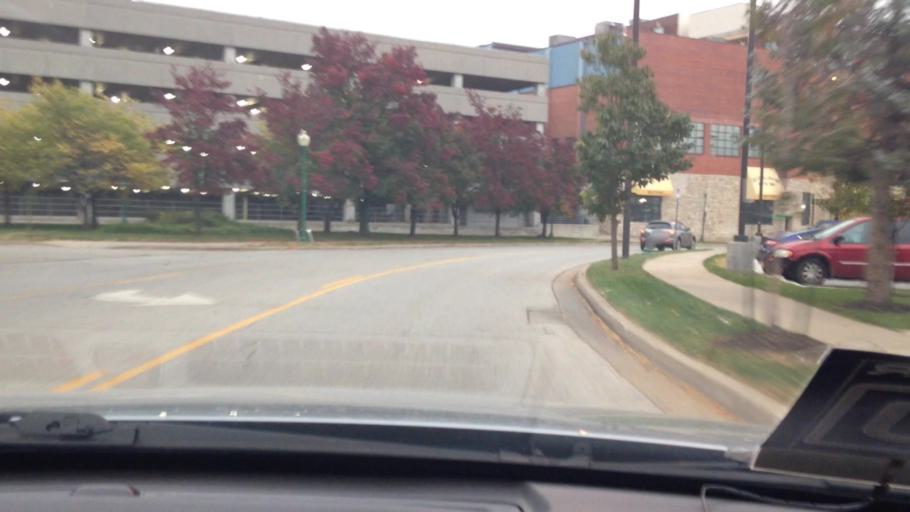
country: US
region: Kansas
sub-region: Johnson County
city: Westwood
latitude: 39.0535
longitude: -94.5938
